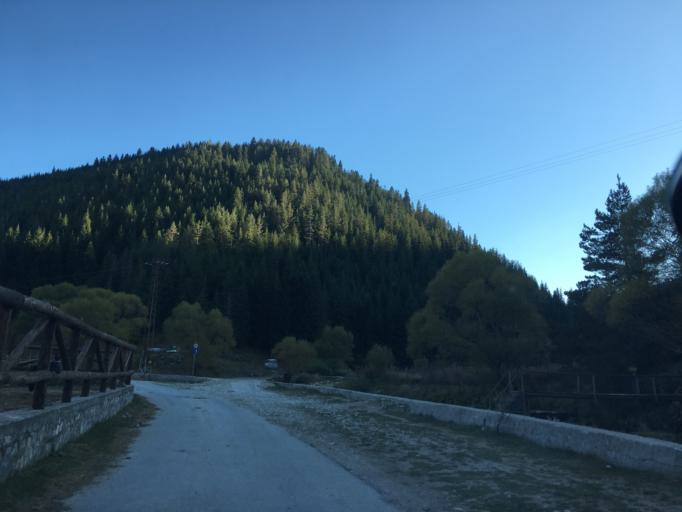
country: BG
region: Smolyan
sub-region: Obshtina Borino
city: Borino
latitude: 41.5834
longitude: 24.3930
